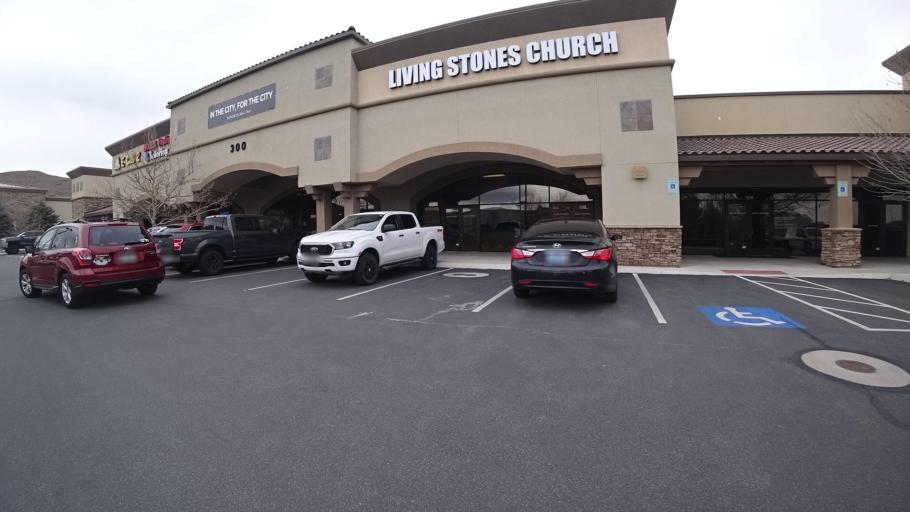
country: US
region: Nevada
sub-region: Washoe County
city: Sun Valley
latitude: 39.5850
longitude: -119.7398
